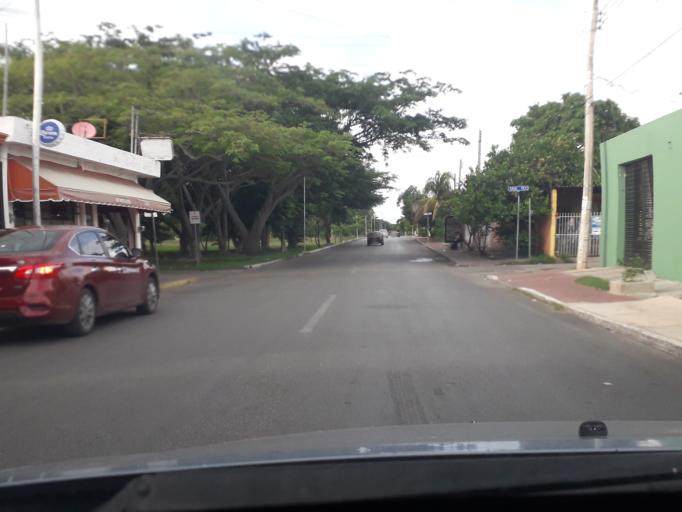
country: MX
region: Yucatan
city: Merida
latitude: 20.9753
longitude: -89.6631
